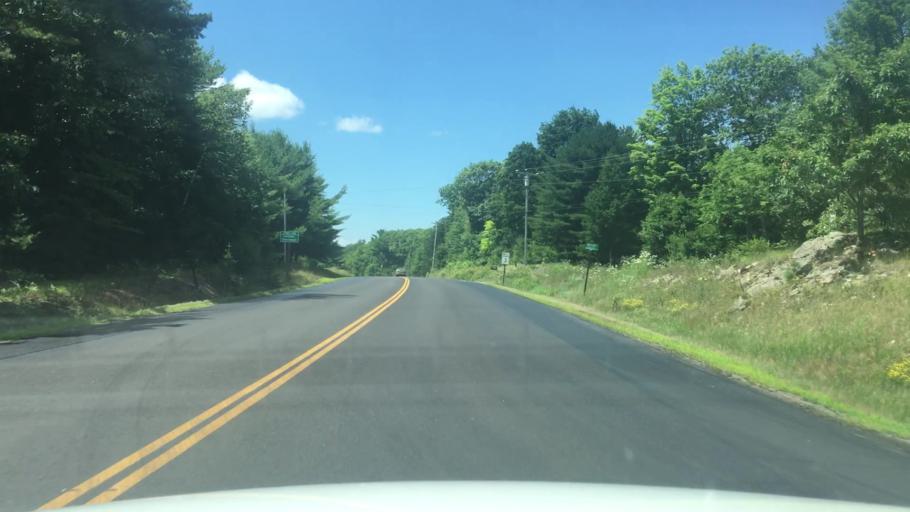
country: US
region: Maine
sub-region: Waldo County
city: Searsmont
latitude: 44.4105
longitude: -69.1847
